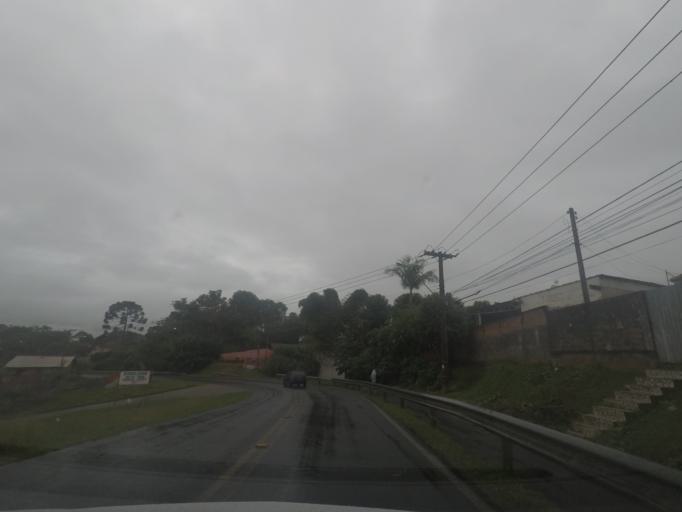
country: BR
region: Parana
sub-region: Quatro Barras
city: Quatro Barras
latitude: -25.3750
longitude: -49.1118
